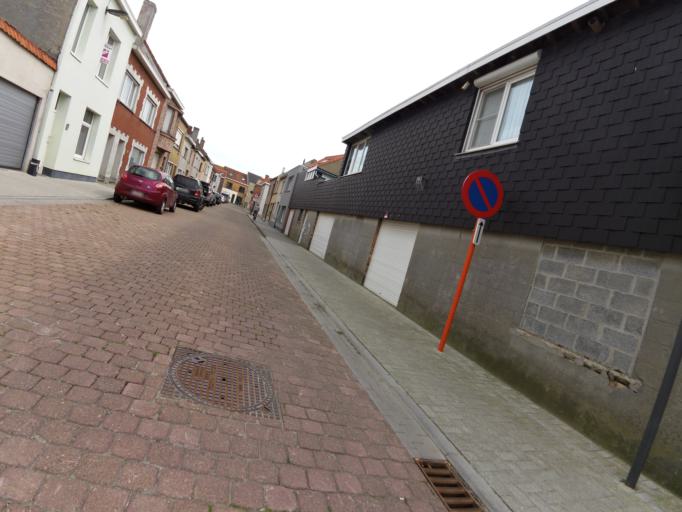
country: BE
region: Flanders
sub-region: Provincie West-Vlaanderen
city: Bredene
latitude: 51.2231
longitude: 2.9568
